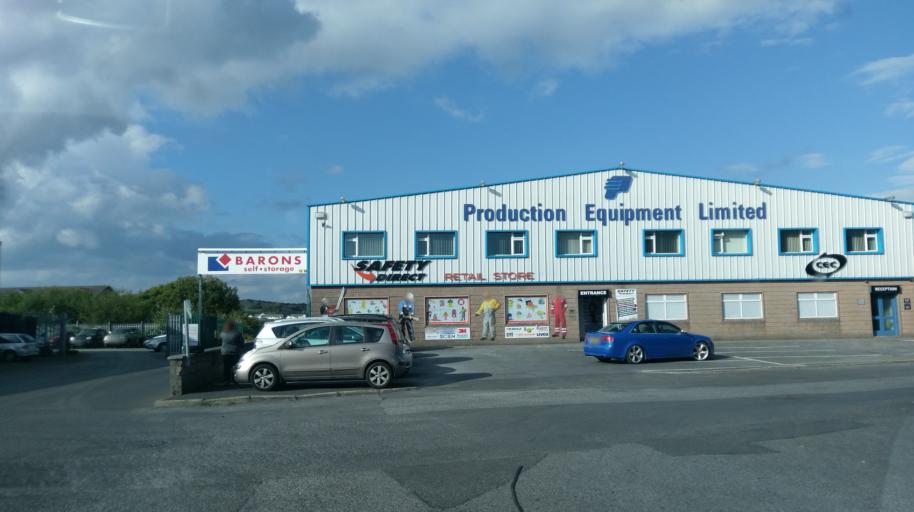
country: IE
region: Connaught
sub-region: County Galway
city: Gaillimh
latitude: 53.2893
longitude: -9.0258
